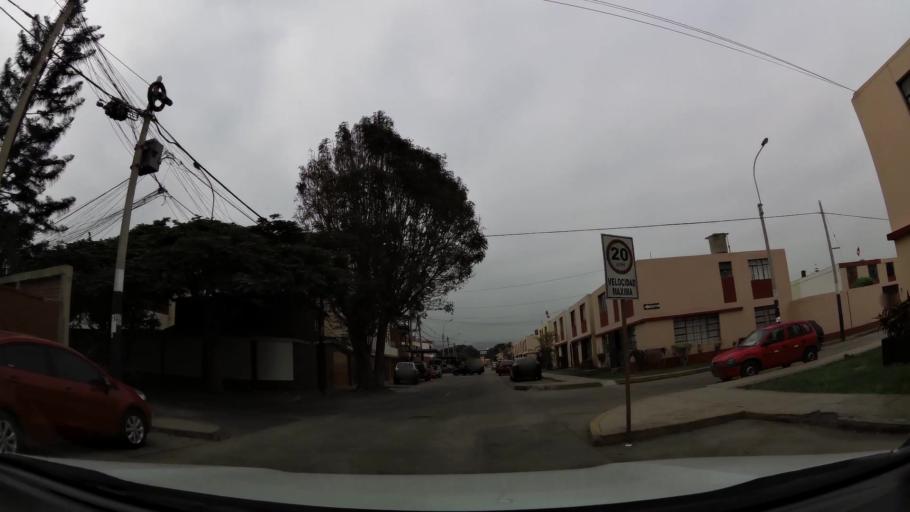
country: PE
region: Lima
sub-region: Lima
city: Surco
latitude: -12.1575
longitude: -77.0220
